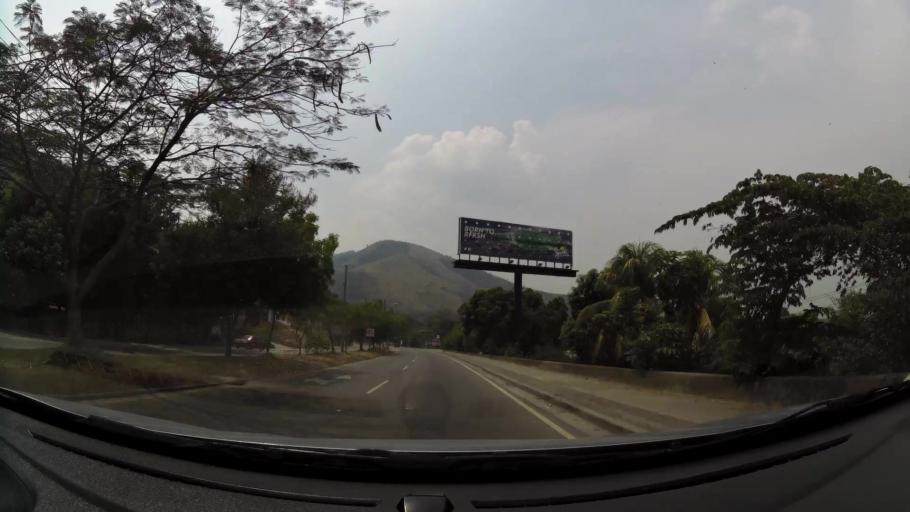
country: HN
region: Cortes
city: Chotepe
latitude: 15.4231
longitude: -88.0200
